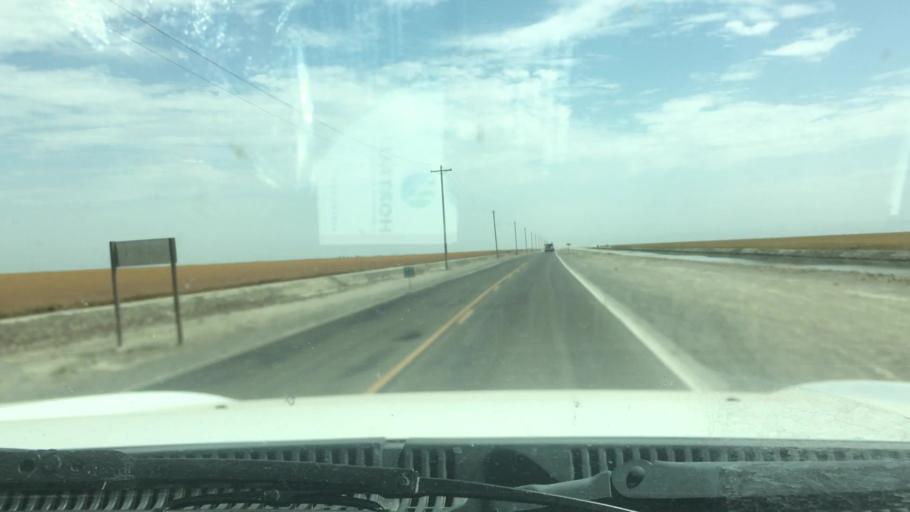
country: US
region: California
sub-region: Tulare County
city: Alpaugh
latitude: 35.9340
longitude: -119.5731
